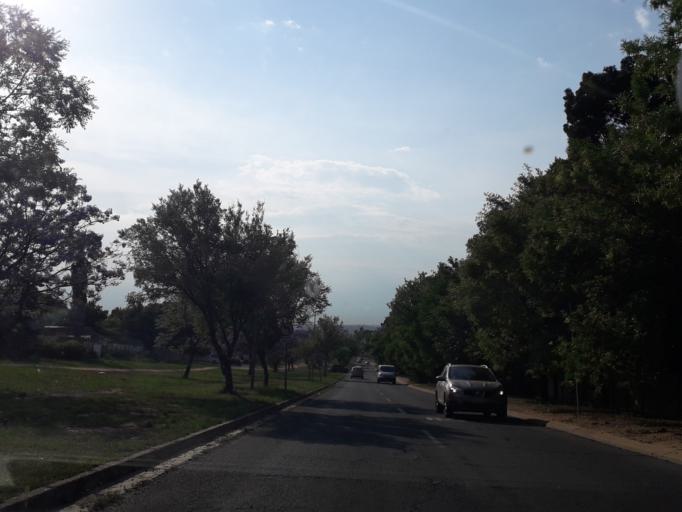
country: ZA
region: Gauteng
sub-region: City of Johannesburg Metropolitan Municipality
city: Roodepoort
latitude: -26.1108
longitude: 27.9418
